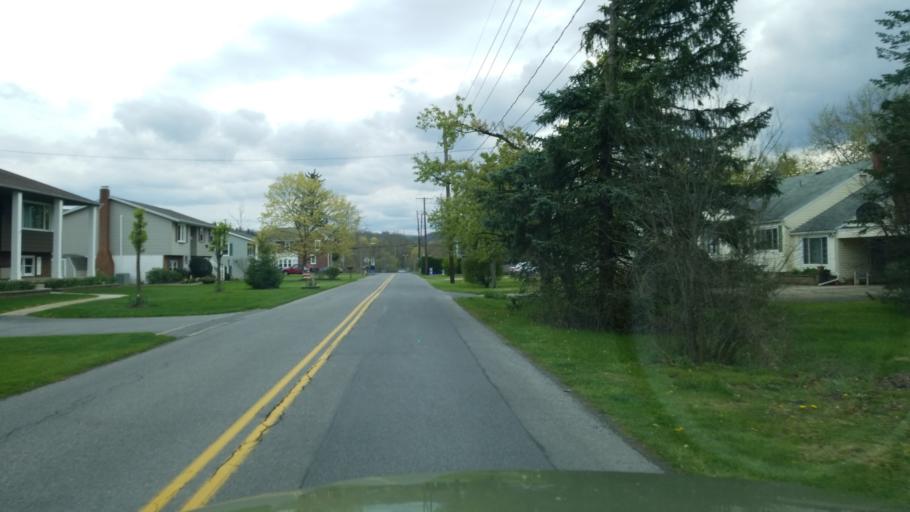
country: US
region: Pennsylvania
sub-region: Blair County
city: Hollidaysburg
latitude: 40.4360
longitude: -78.4044
